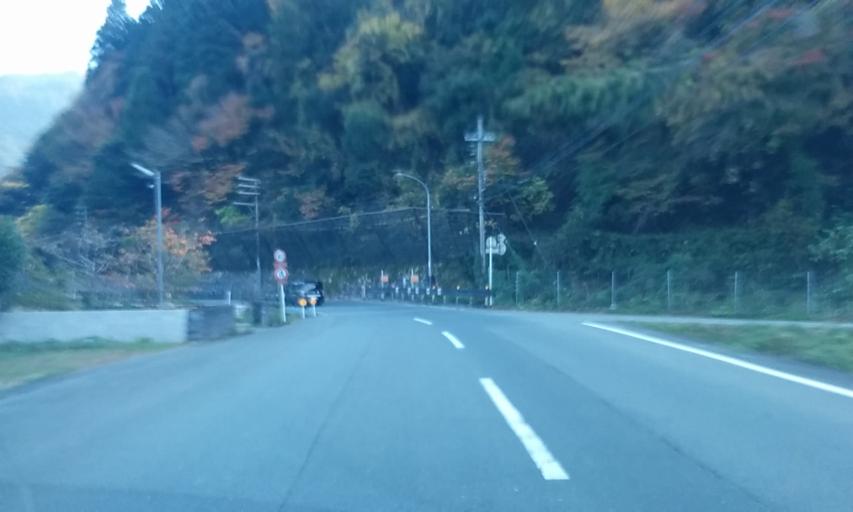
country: JP
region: Fukui
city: Obama
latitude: 35.3087
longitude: 135.6215
